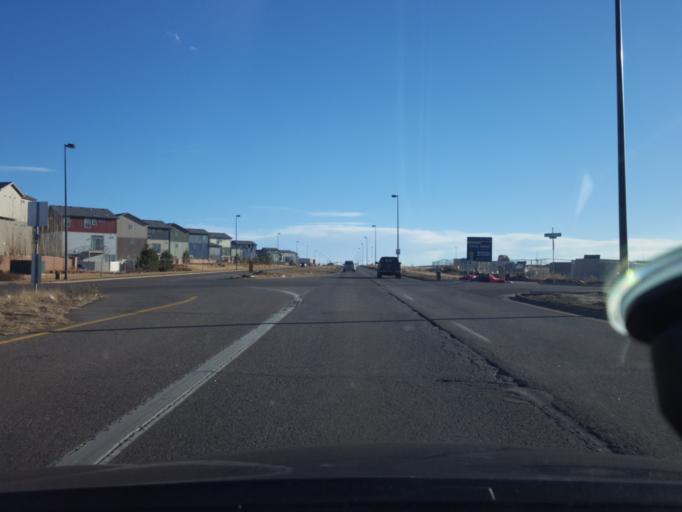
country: US
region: Colorado
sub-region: Adams County
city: Aurora
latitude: 39.7931
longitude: -104.7722
